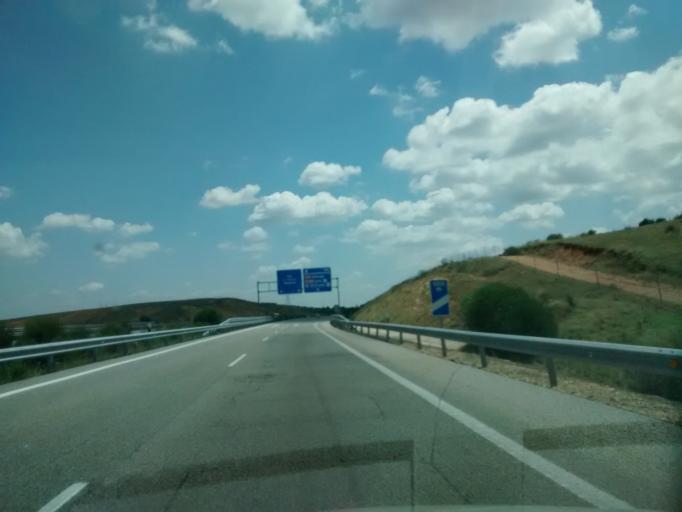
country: ES
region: Castille and Leon
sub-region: Provincia de Leon
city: Astorga
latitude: 42.4385
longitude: -6.0587
